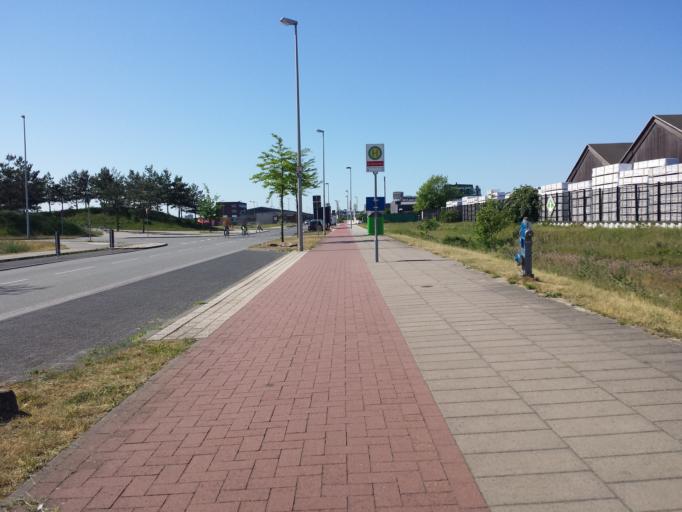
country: DE
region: Bremen
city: Bremen
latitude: 53.1006
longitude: 8.7642
